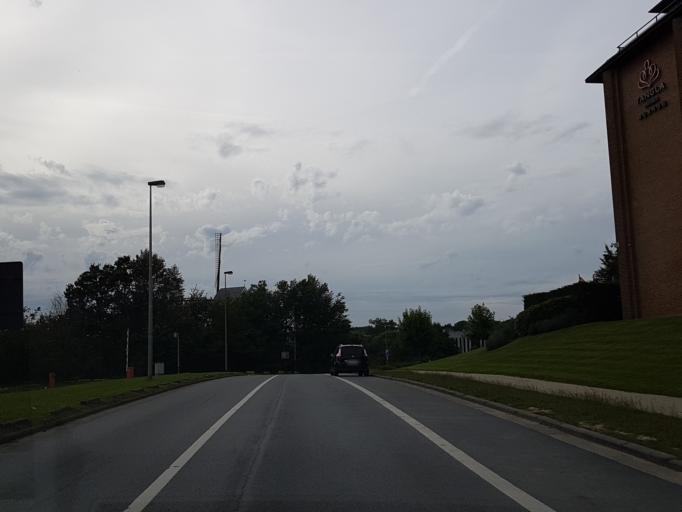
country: BE
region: Flanders
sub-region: Provincie Vlaams-Brabant
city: Kraainem
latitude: 50.8523
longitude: 4.4485
